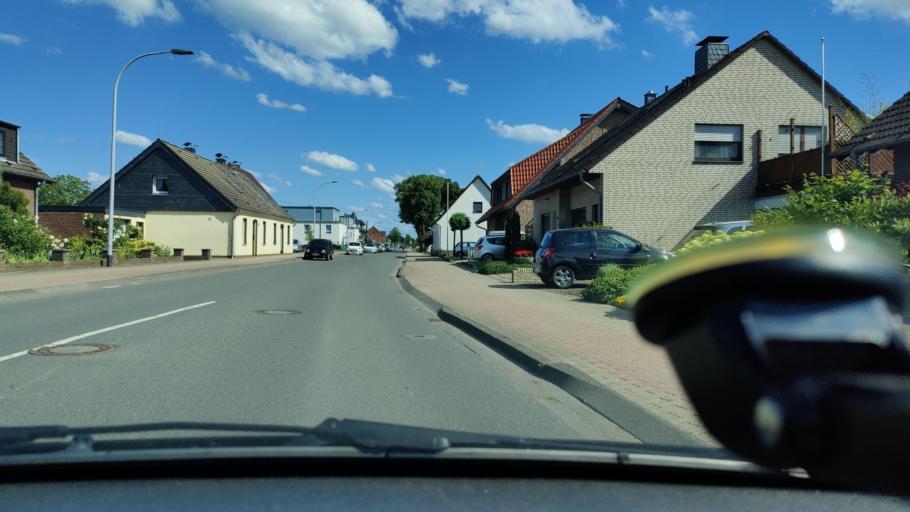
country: DE
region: North Rhine-Westphalia
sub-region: Regierungsbezirk Dusseldorf
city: Alpen
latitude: 51.5613
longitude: 6.5429
